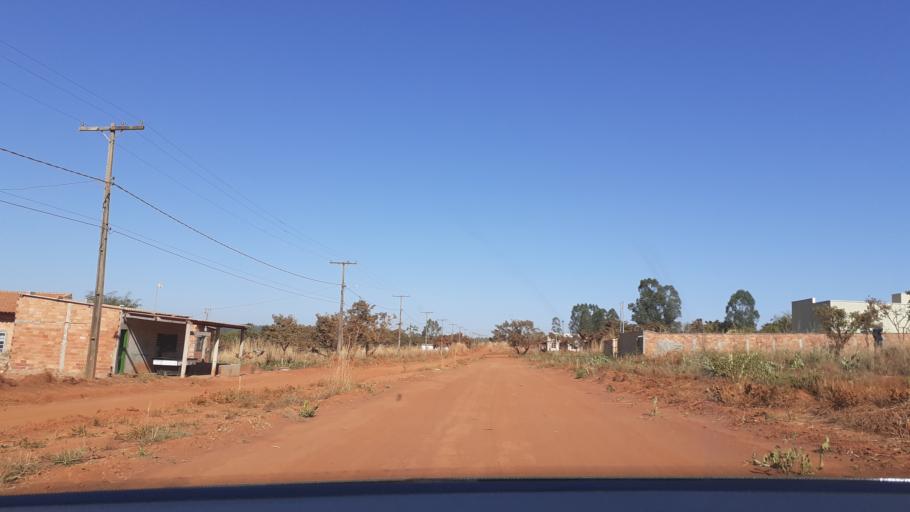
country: BR
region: Goias
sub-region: Aparecida De Goiania
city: Aparecida de Goiania
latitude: -16.8734
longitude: -49.2757
